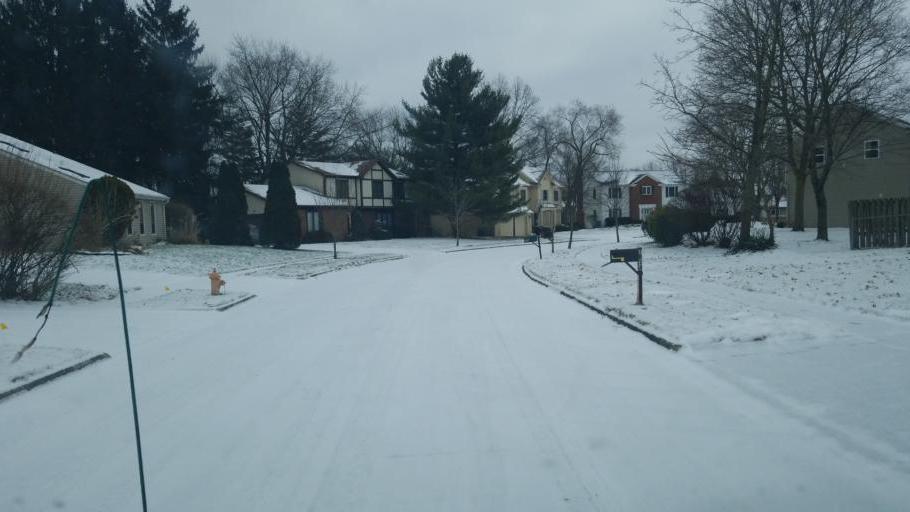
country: US
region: Ohio
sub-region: Delaware County
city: Powell
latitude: 40.1261
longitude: -83.0796
